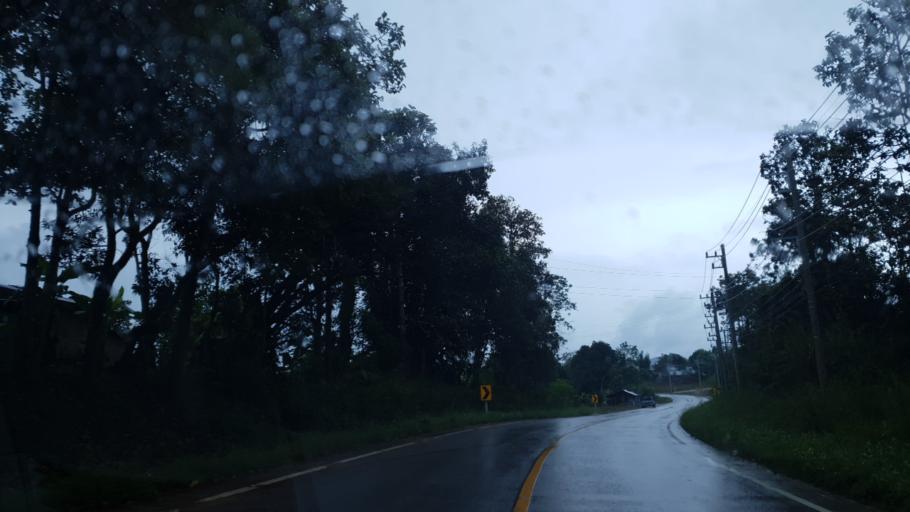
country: TH
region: Mae Hong Son
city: Pa Pae
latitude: 18.1584
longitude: 98.2859
